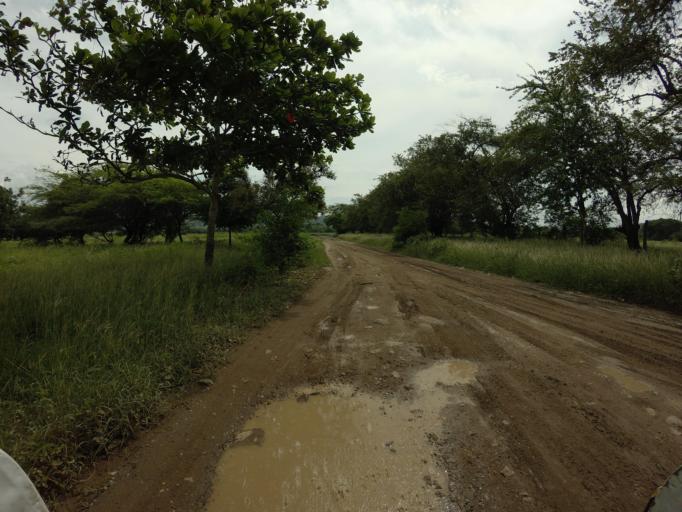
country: CO
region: Tolima
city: Natagaima
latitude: 3.4491
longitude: -75.1412
